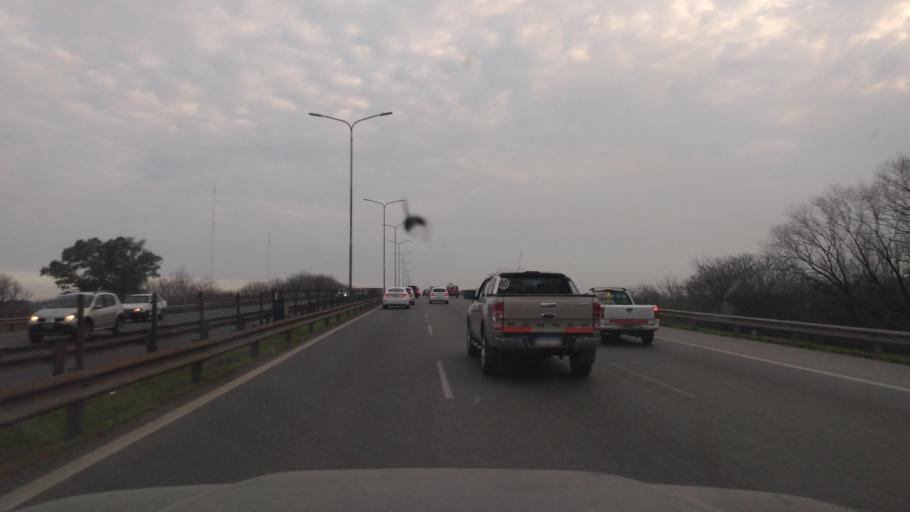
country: AR
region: Buenos Aires
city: Hurlingham
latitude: -34.5734
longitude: -58.6636
